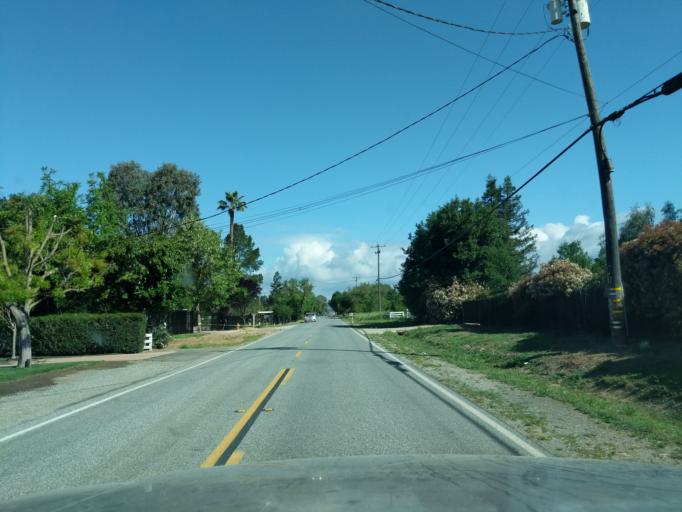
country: US
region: California
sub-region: Santa Clara County
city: San Martin
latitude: 37.0894
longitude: -121.5786
